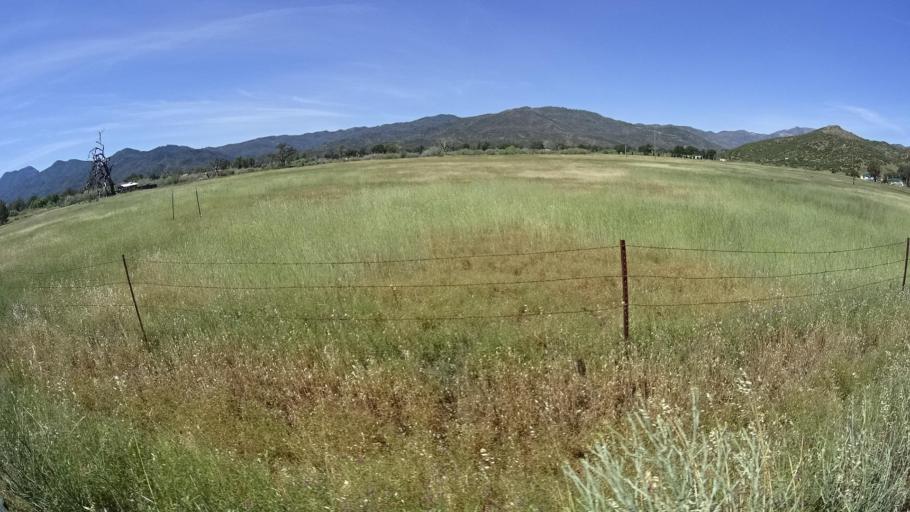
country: US
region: California
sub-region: Lake County
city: Middletown
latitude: 38.7646
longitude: -122.6188
